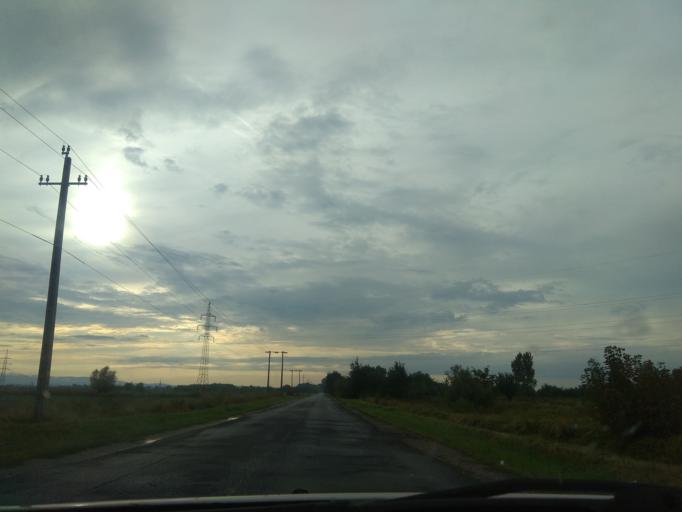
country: HU
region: Borsod-Abauj-Zemplen
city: Onga
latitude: 48.1156
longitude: 20.9389
